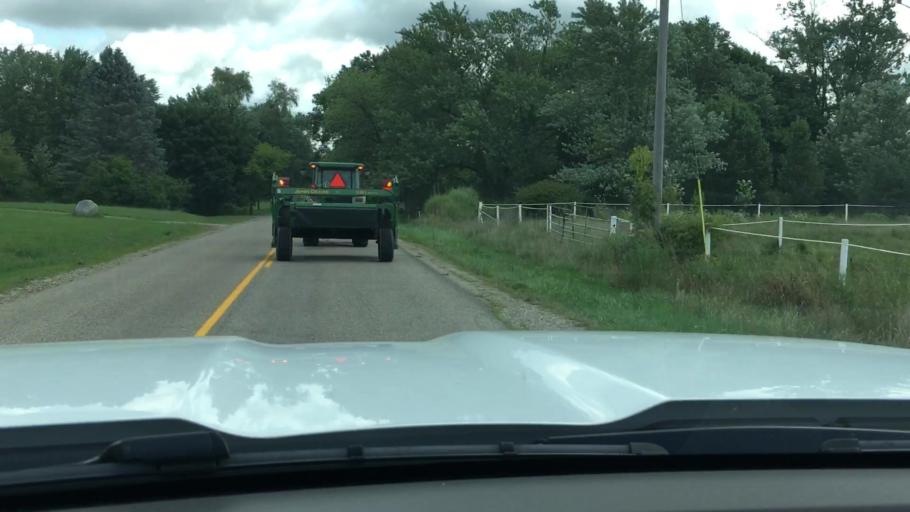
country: US
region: Michigan
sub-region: Eaton County
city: Dimondale
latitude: 42.5821
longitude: -84.6135
